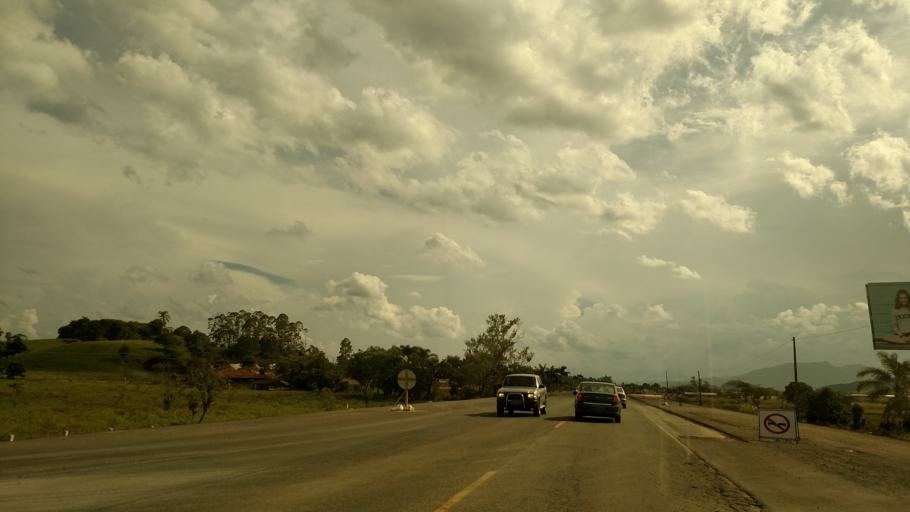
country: BR
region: Santa Catarina
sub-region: Itajai
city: Itajai
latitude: -26.9696
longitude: -48.7845
